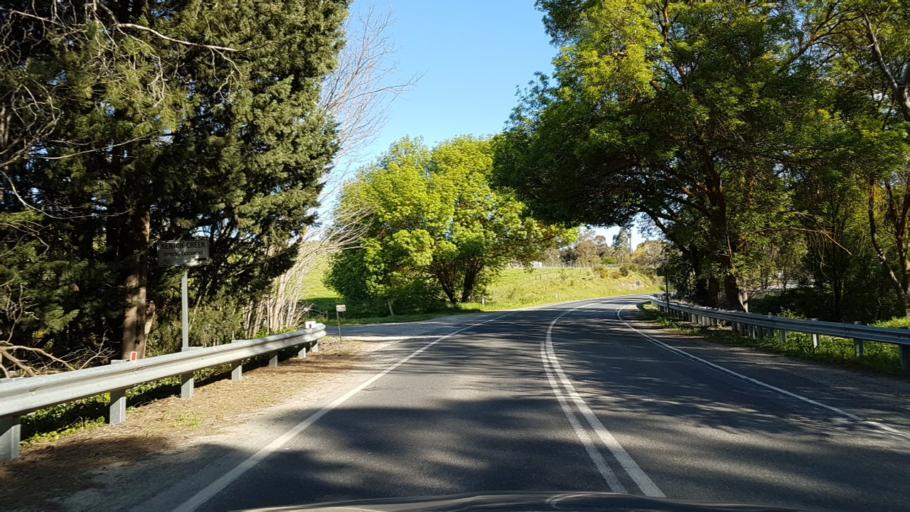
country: AU
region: South Australia
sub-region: Adelaide Hills
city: Gumeracha
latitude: -34.8300
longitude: 138.8909
